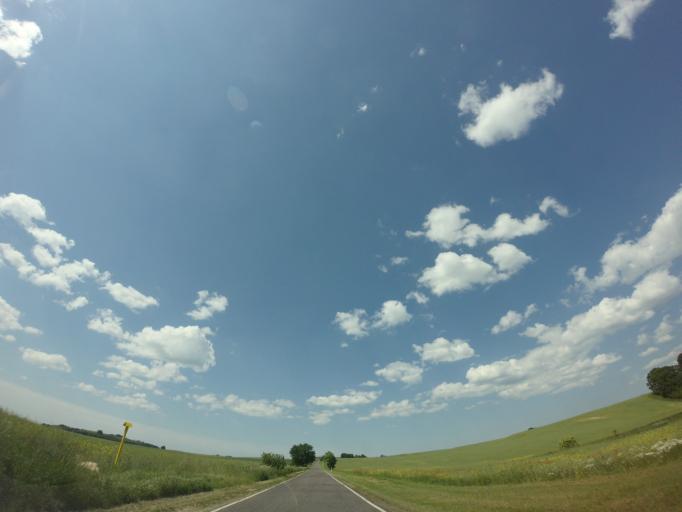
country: PL
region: West Pomeranian Voivodeship
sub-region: Powiat choszczenski
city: Pelczyce
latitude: 53.1014
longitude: 15.2621
